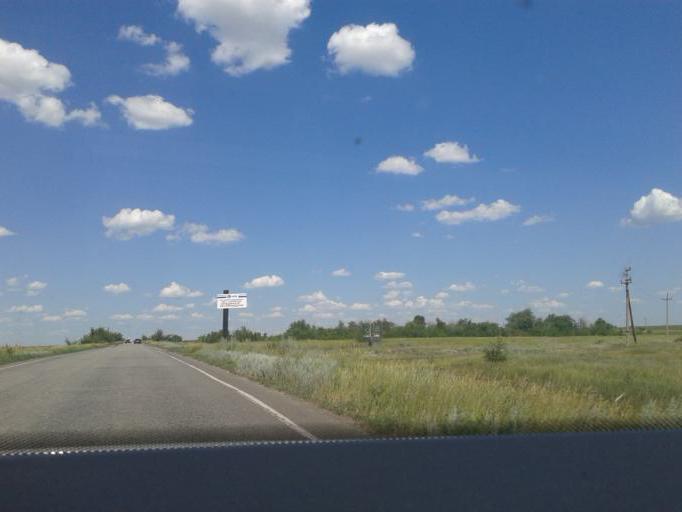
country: RU
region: Volgograd
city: Frolovo
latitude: 49.6841
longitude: 43.6400
